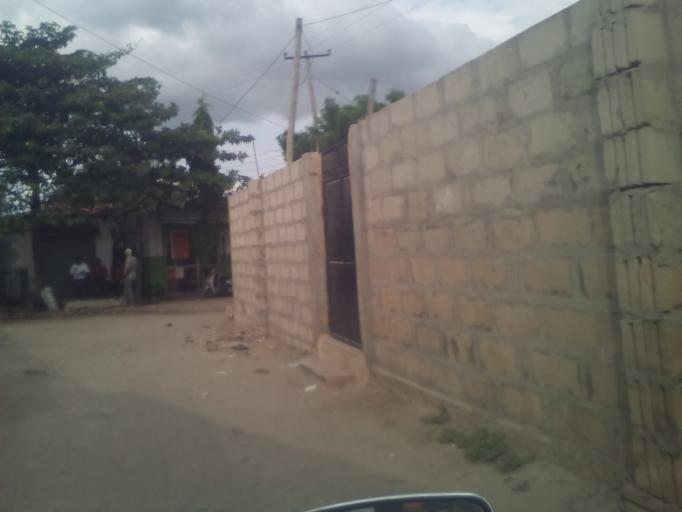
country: TZ
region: Dar es Salaam
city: Dar es Salaam
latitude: -6.8428
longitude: 39.2736
